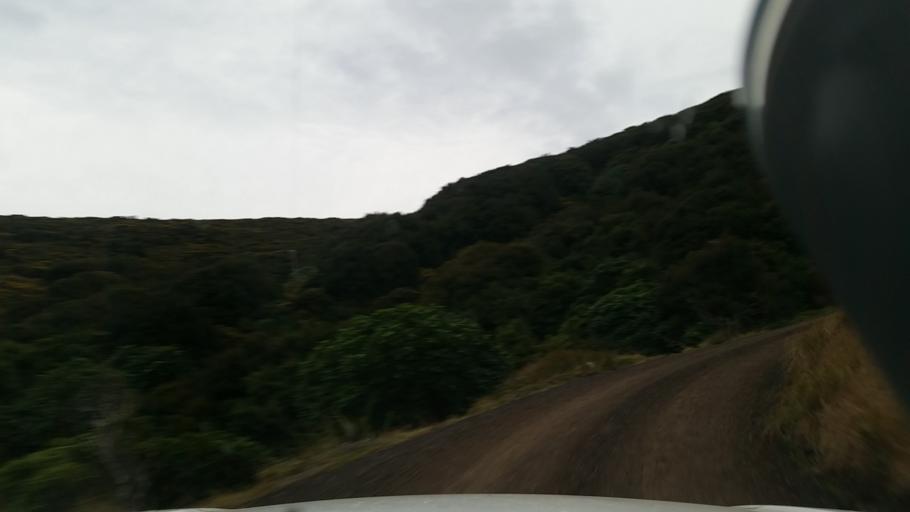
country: NZ
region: Canterbury
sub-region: Christchurch City
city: Christchurch
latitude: -43.8456
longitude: 172.9770
